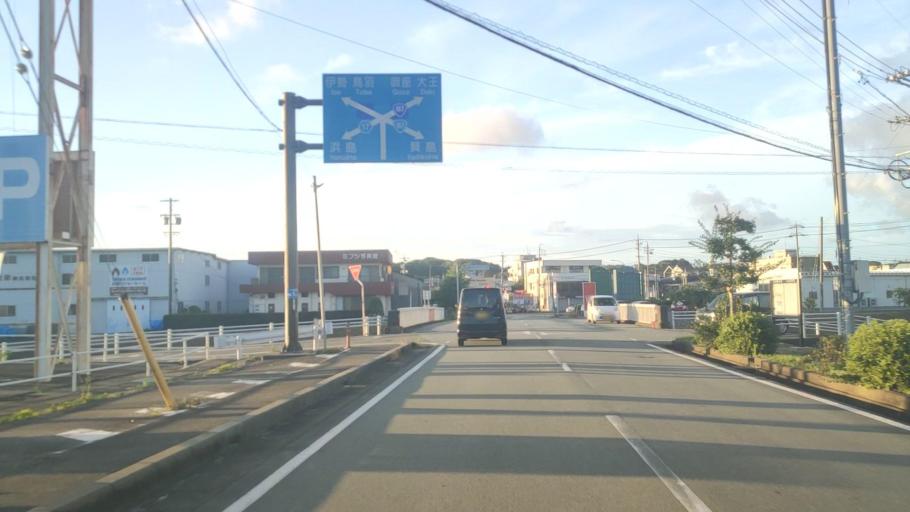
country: JP
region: Mie
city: Toba
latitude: 34.3276
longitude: 136.8220
